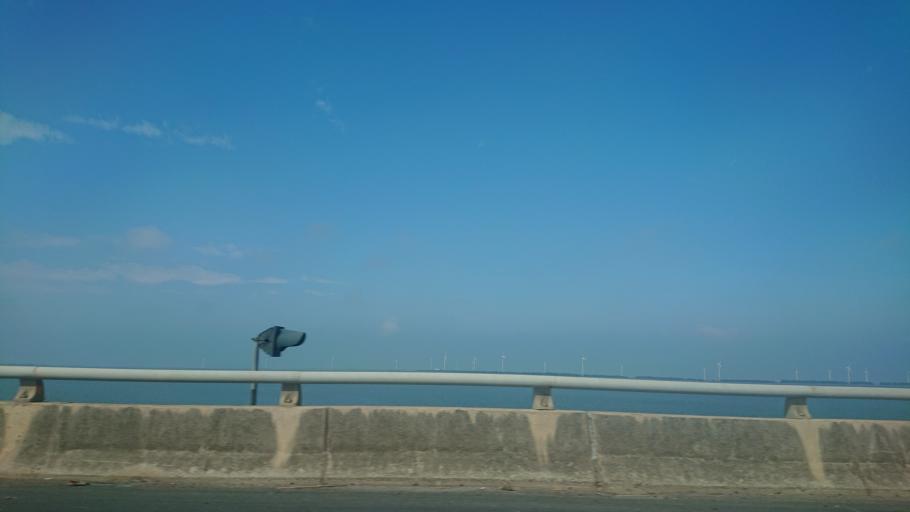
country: TW
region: Taiwan
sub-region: Changhua
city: Chang-hua
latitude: 24.0937
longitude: 120.4320
